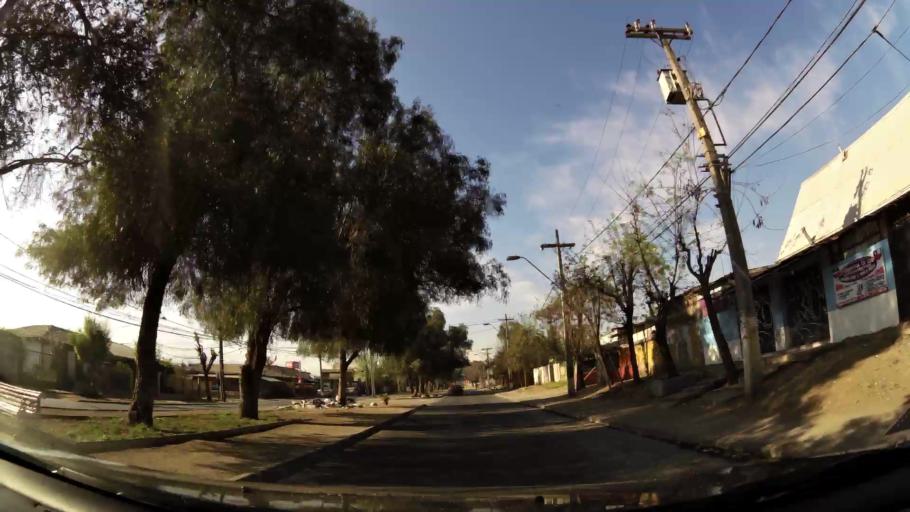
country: CL
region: Santiago Metropolitan
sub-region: Provincia de Santiago
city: Lo Prado
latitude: -33.3952
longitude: -70.6817
